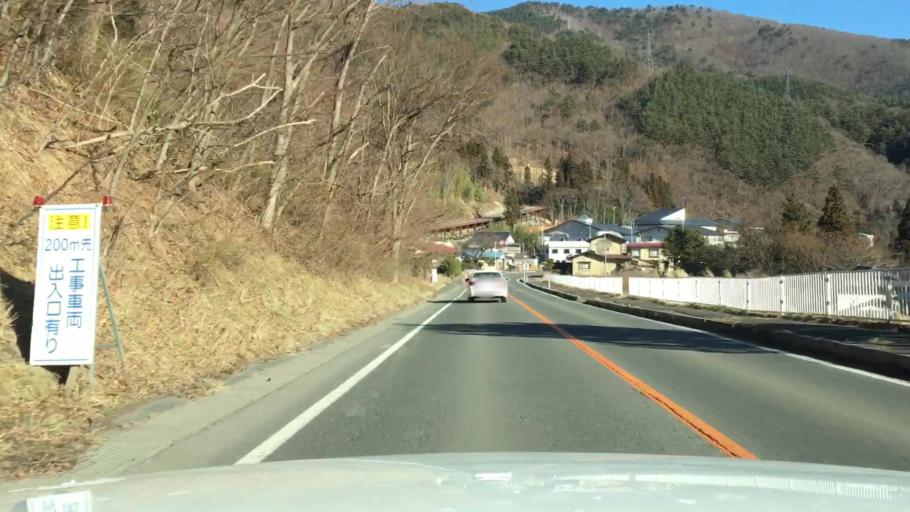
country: JP
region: Iwate
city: Miyako
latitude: 39.5967
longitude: 141.6770
